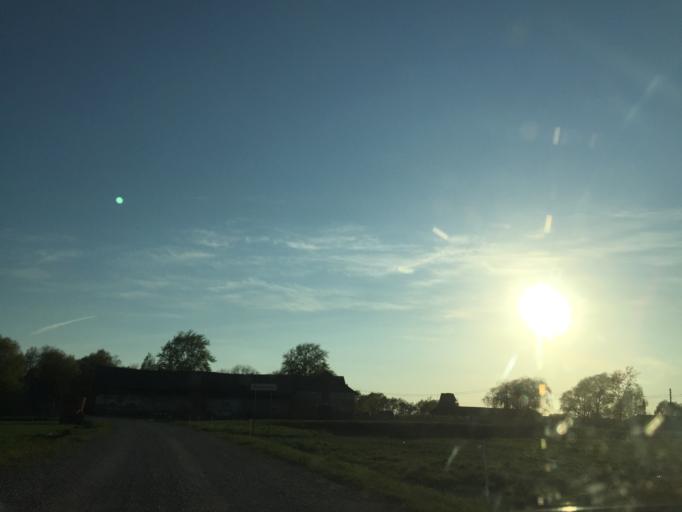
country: LV
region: Bauskas Rajons
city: Bauska
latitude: 56.2886
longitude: 24.1907
